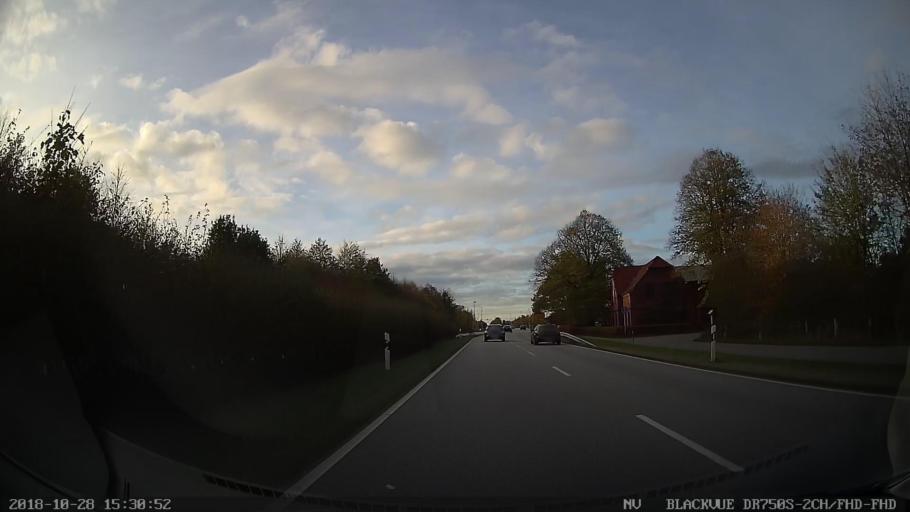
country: DE
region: Schleswig-Holstein
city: Kolln-Reisiek
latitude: 53.7455
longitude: 9.7008
